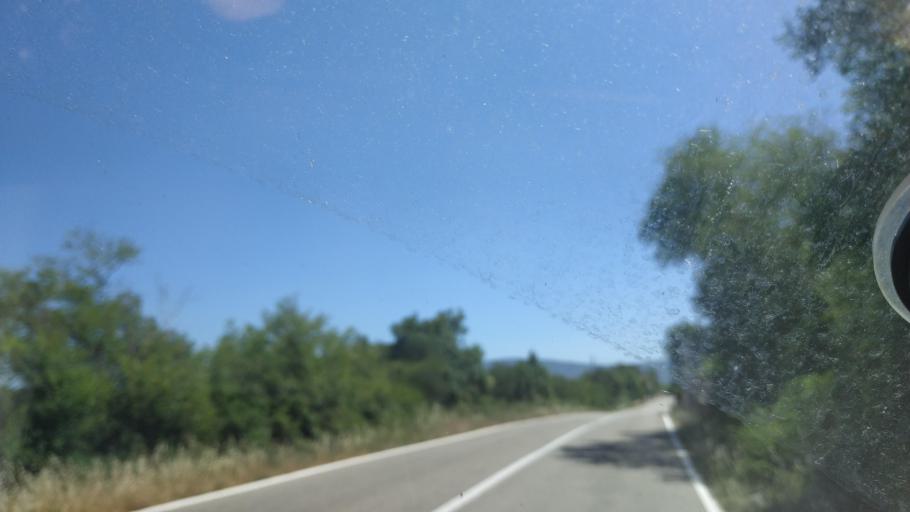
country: HR
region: Sibensko-Kniniska
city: Drnis
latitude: 43.8954
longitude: 16.2103
